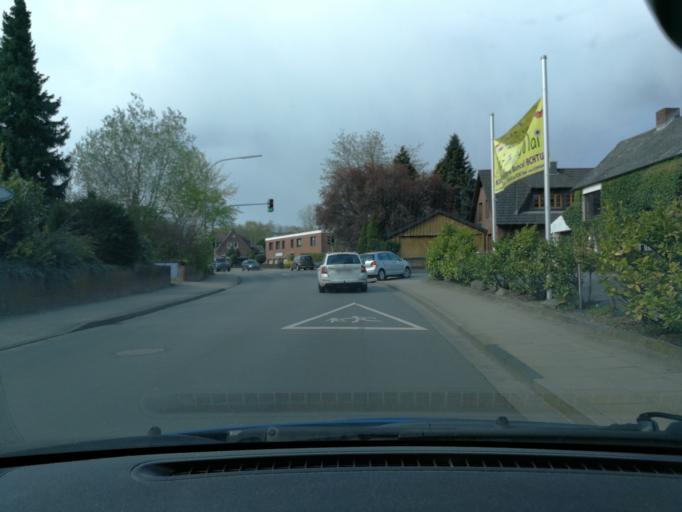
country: DE
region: Hamburg
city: Harburg
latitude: 53.4234
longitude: 10.0205
